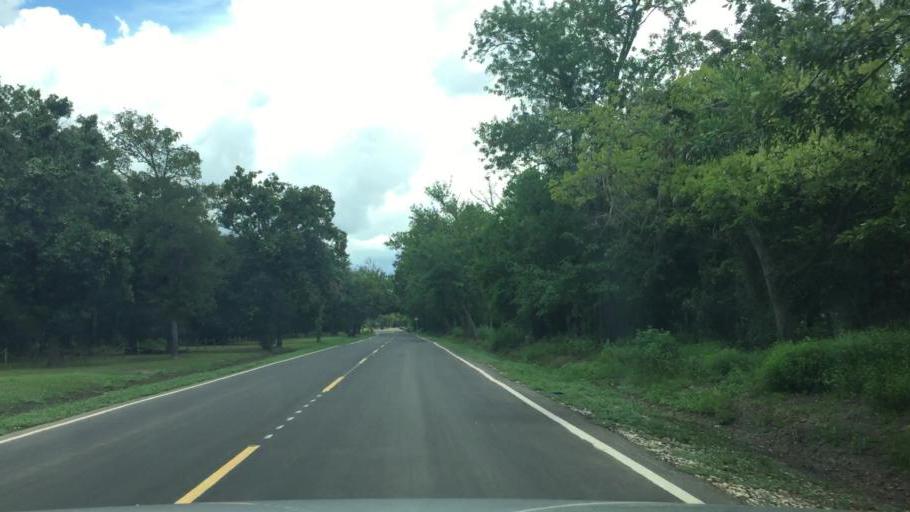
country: US
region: Texas
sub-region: Harris County
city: Jersey Village
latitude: 29.8133
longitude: -95.6318
